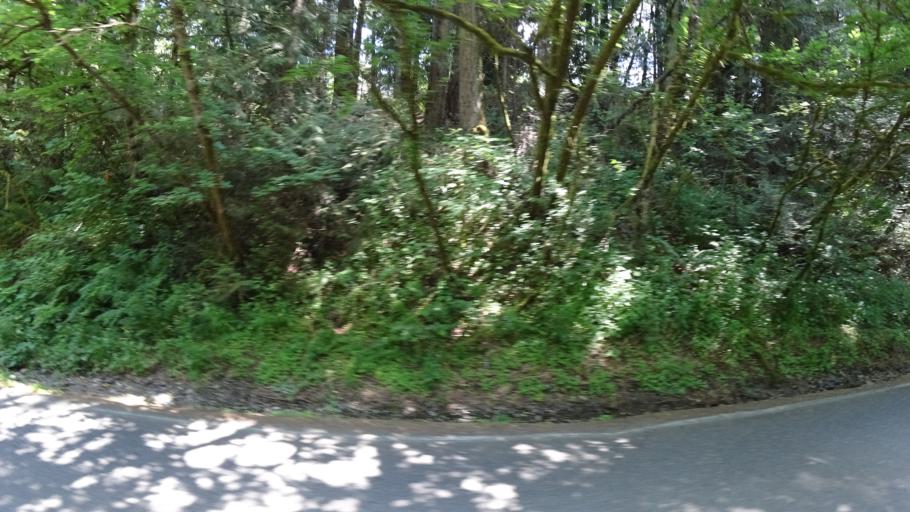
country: US
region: Oregon
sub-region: Clackamas County
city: Happy Valley
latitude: 45.4735
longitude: -122.5146
